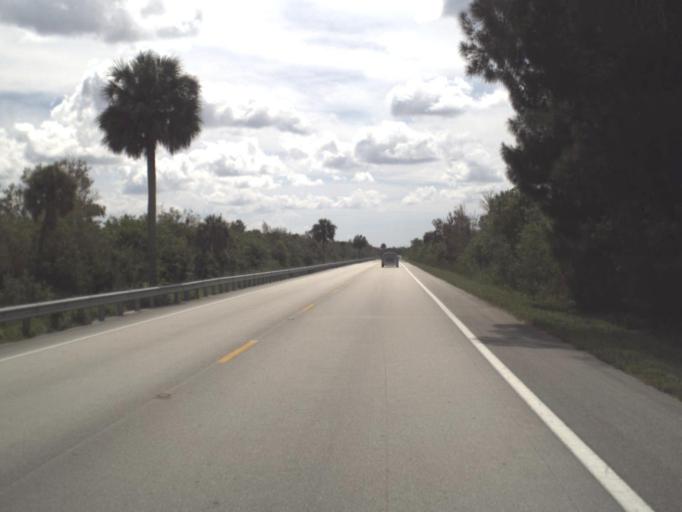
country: US
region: Florida
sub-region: Collier County
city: Lely Resort
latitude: 25.9323
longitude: -81.3574
